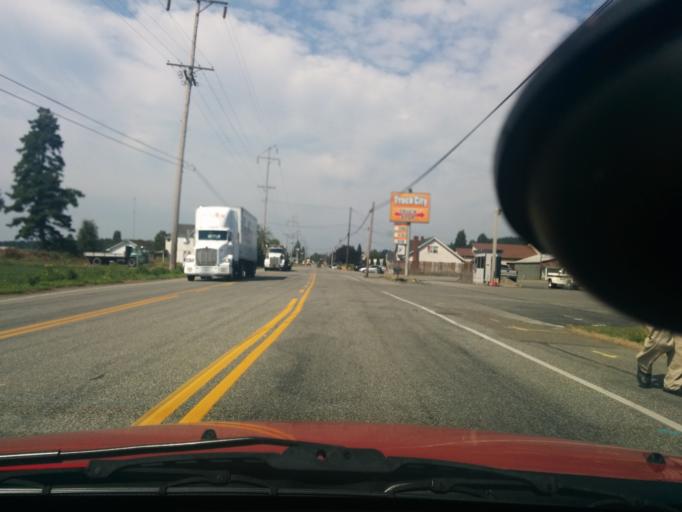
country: US
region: Washington
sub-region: Skagit County
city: Mount Vernon
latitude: 48.3942
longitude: -122.3356
